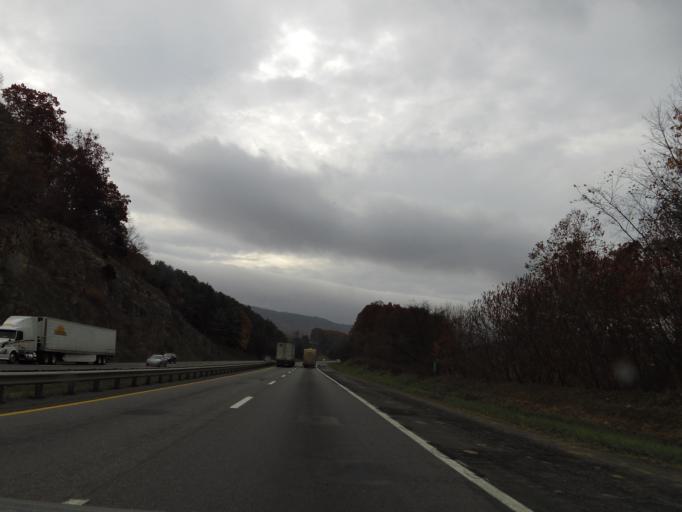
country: US
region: Virginia
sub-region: Bland County
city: Bland
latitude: 37.0717
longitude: -81.1268
